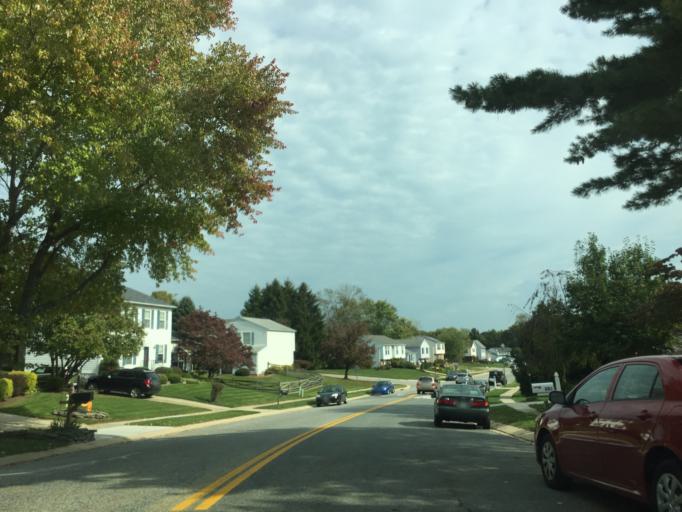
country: US
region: Maryland
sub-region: Harford County
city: Bel Air South
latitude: 39.4786
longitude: -76.3020
